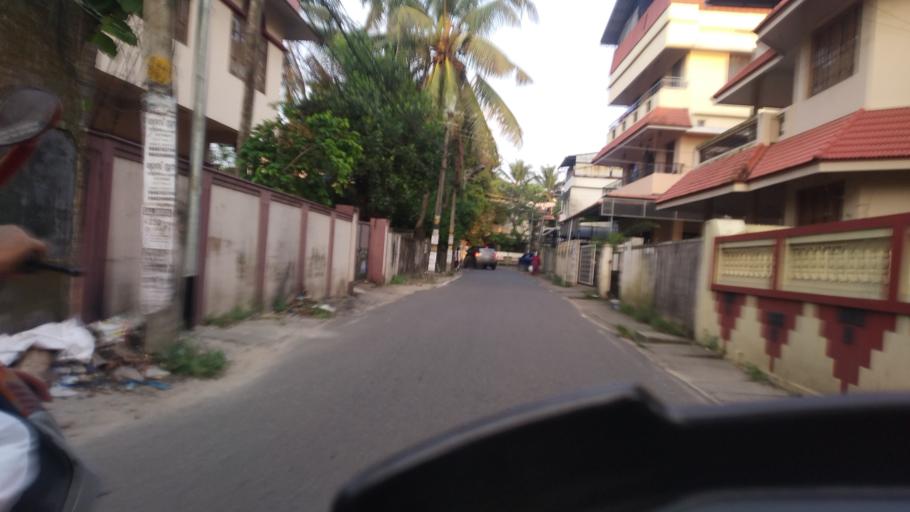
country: IN
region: Kerala
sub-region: Ernakulam
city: Elur
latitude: 10.0318
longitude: 76.3021
